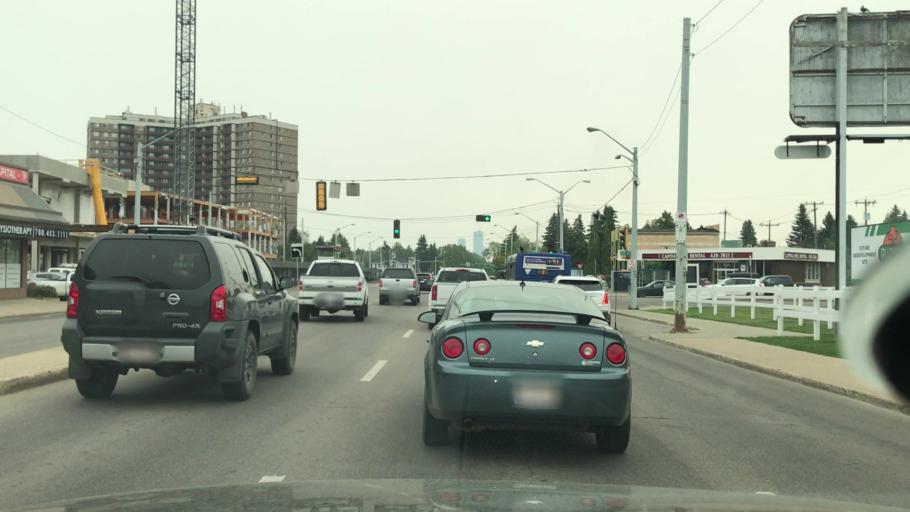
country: CA
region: Alberta
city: Edmonton
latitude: 53.5428
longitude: -113.5667
